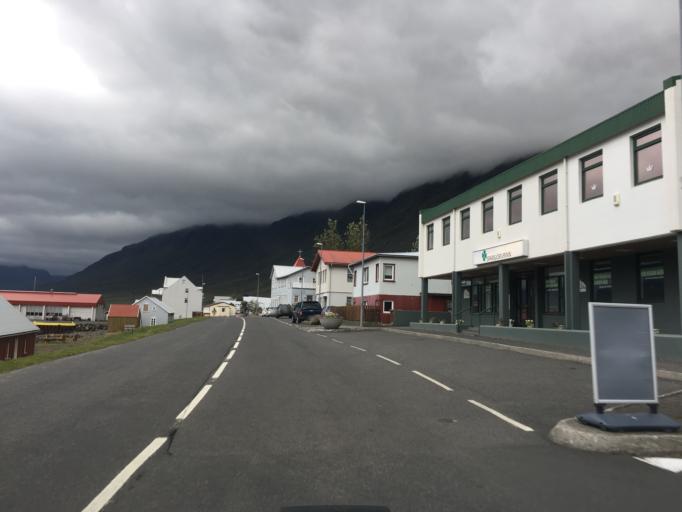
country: IS
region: East
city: Neskaupstadur
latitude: 65.1475
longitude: -13.6829
